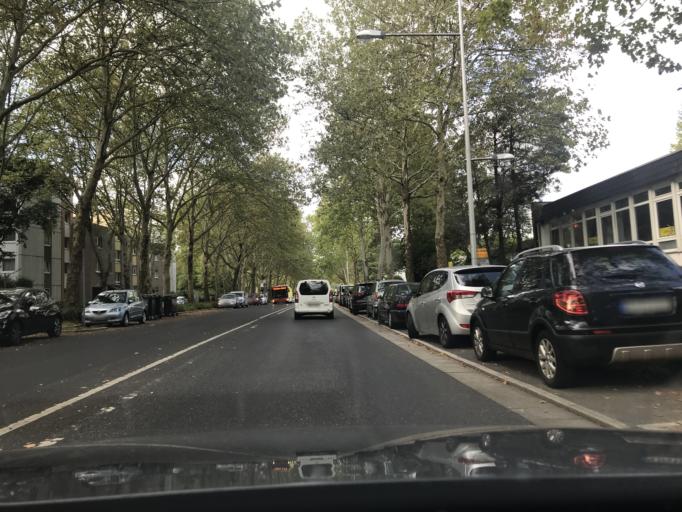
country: DE
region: North Rhine-Westphalia
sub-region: Regierungsbezirk Dusseldorf
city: Mettmann
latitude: 51.2153
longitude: 6.9555
